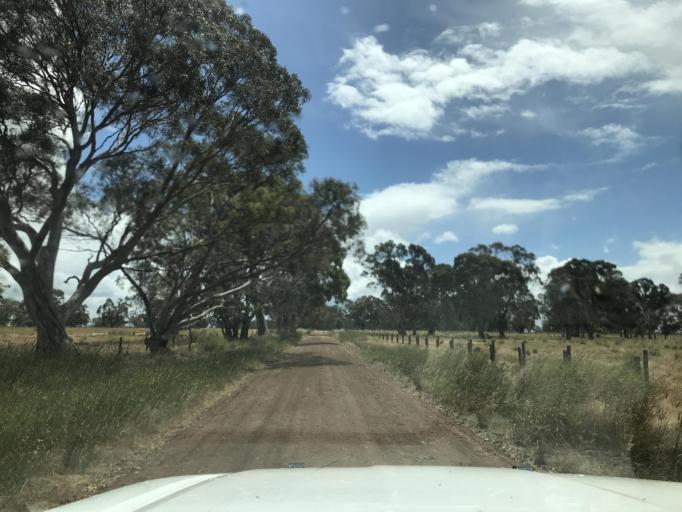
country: AU
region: South Australia
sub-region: Wattle Range
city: Penola
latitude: -37.1263
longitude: 141.3096
